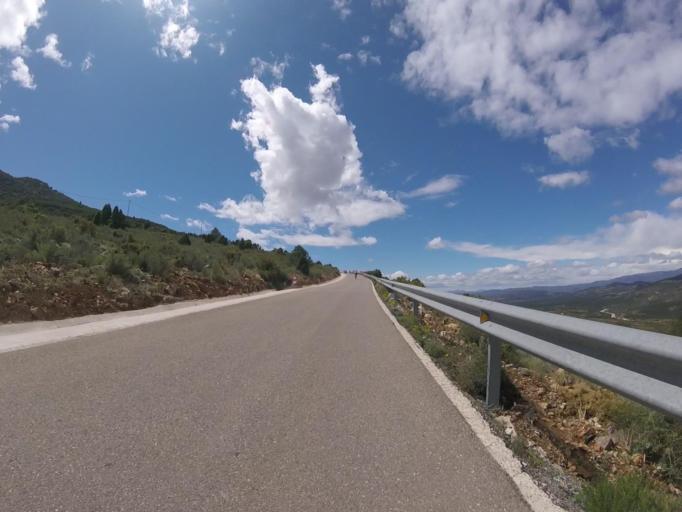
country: ES
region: Valencia
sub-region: Provincia de Castello
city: Sierra-Engarceran
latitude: 40.2930
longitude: -0.0367
